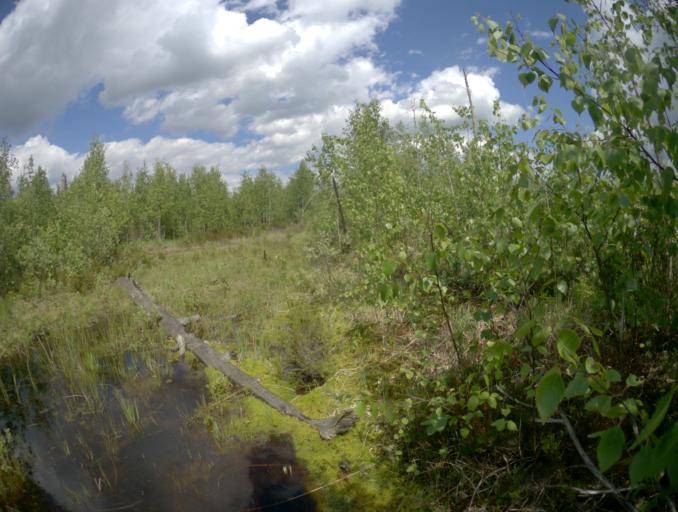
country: RU
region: Vladimir
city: Velikodvorskiy
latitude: 55.2752
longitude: 40.8742
